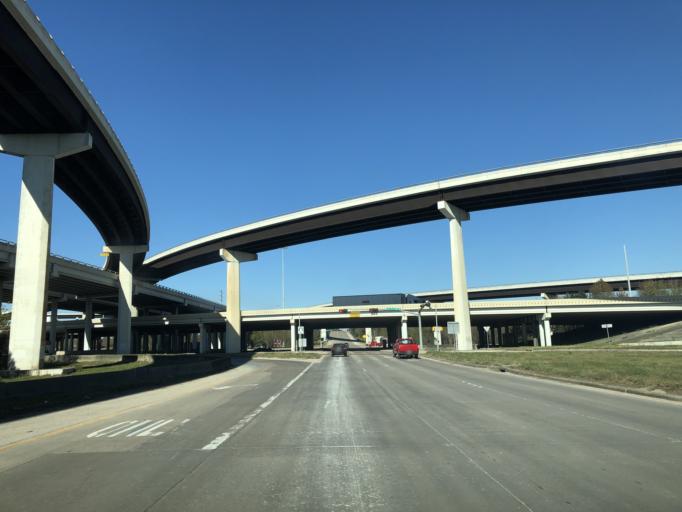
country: US
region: Texas
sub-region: Harris County
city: Cloverleaf
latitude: 29.7704
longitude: -95.1519
